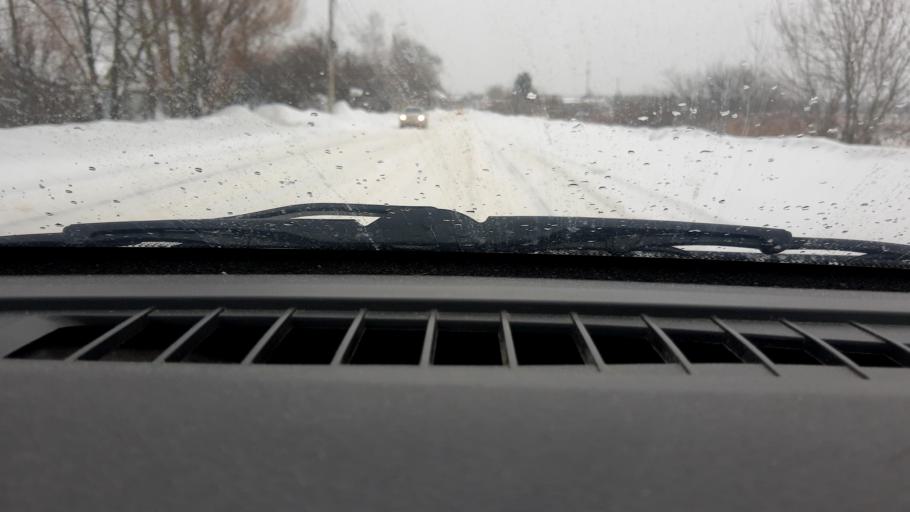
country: RU
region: Moskovskaya
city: Pirogovskiy
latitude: 56.0063
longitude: 37.7231
